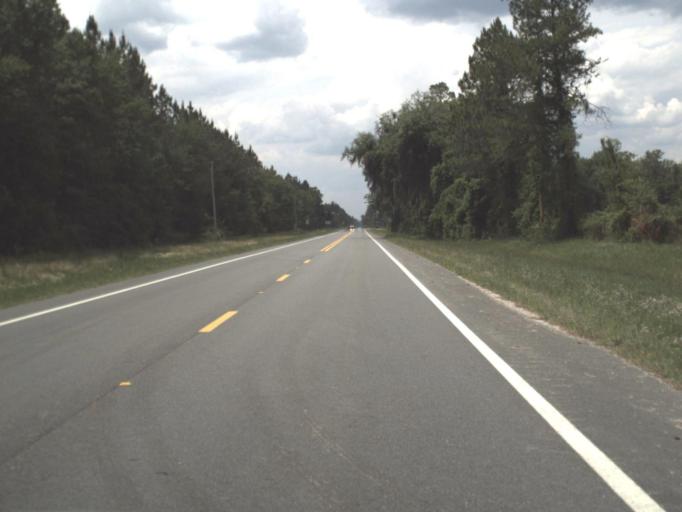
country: US
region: Florida
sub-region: Columbia County
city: Five Points
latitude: 30.4831
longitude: -82.6597
